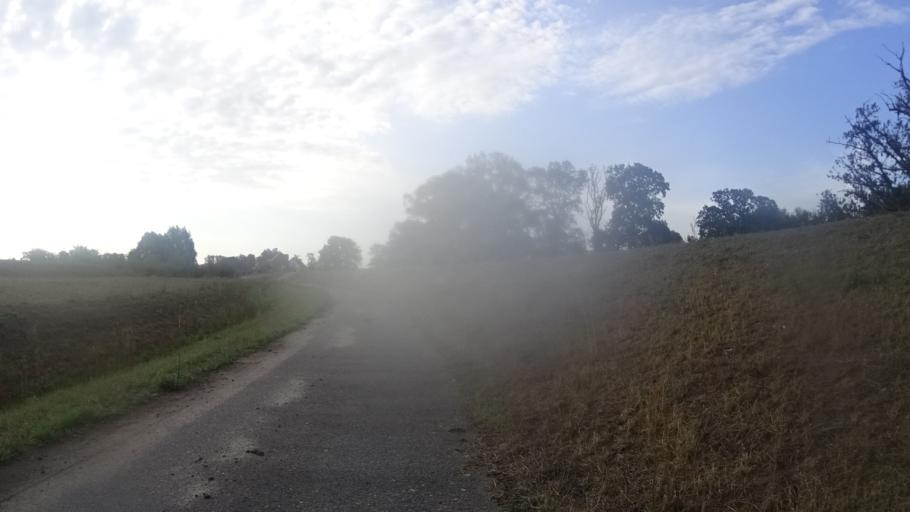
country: DE
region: Brandenburg
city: Lanz
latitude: 53.0401
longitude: 11.5816
